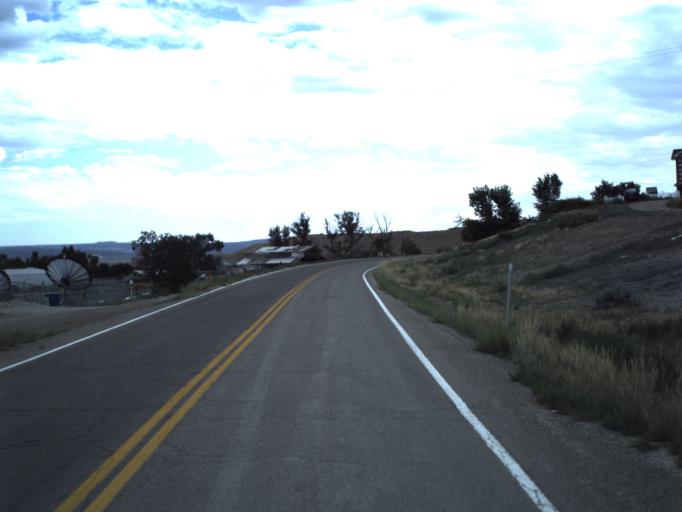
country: US
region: Utah
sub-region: Emery County
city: Huntington
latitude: 39.3703
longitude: -110.8511
